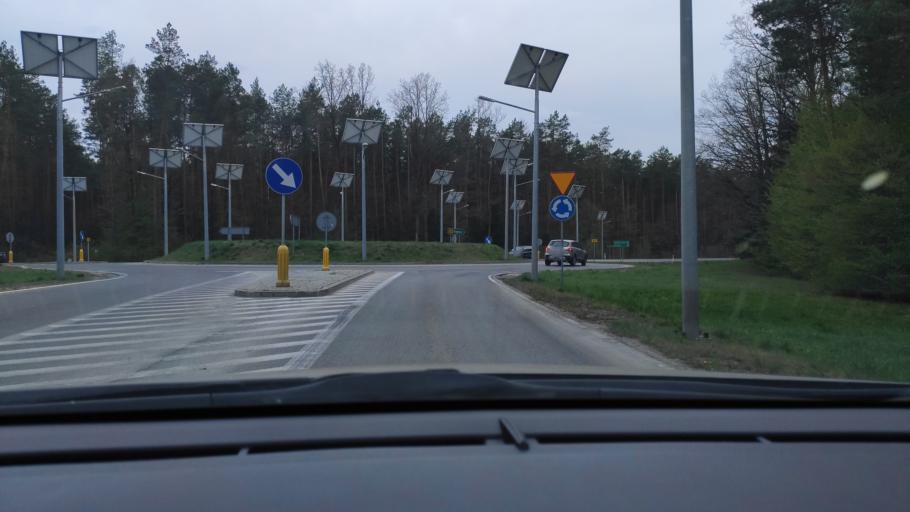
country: PL
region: Masovian Voivodeship
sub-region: Powiat radomski
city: Pionki
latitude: 51.4926
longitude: 21.4225
